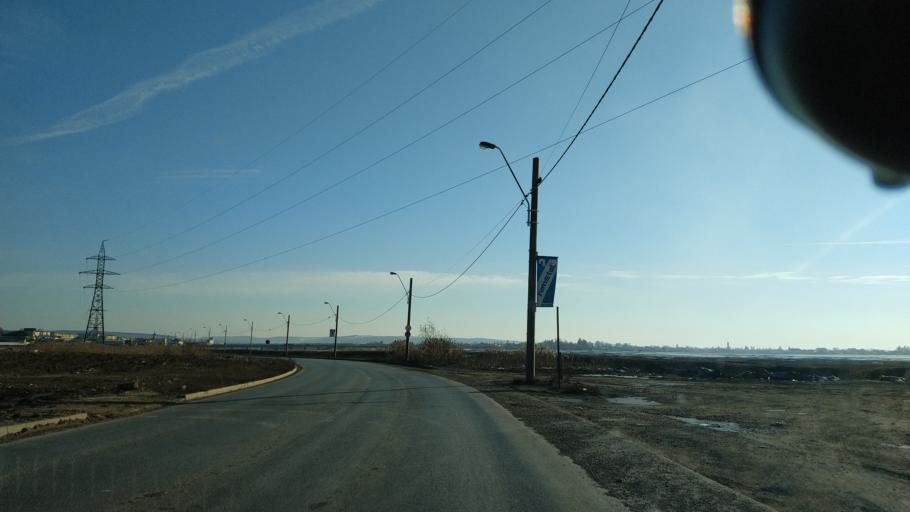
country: RO
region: Neamt
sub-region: Municipiul Roman
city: Roman
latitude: 46.9236
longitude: 26.9103
